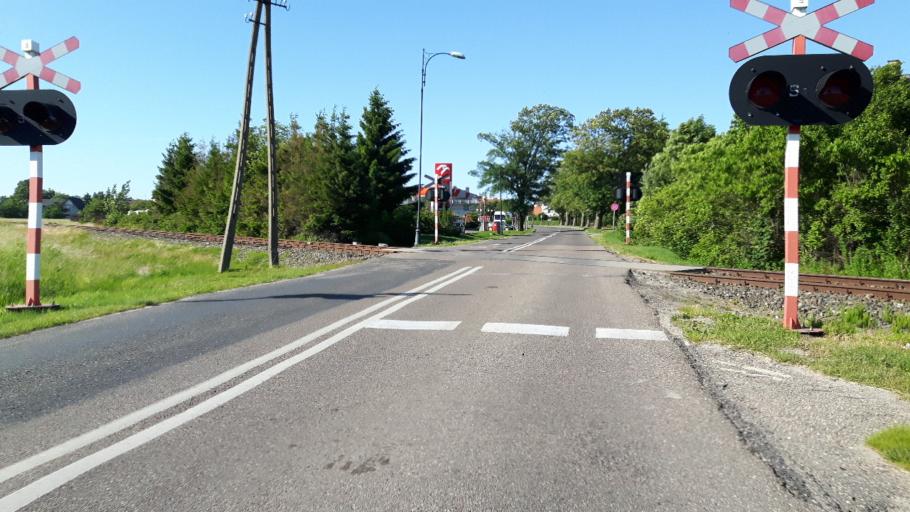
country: PL
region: Pomeranian Voivodeship
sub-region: Powiat leborski
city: Leba
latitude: 54.7506
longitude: 17.5580
